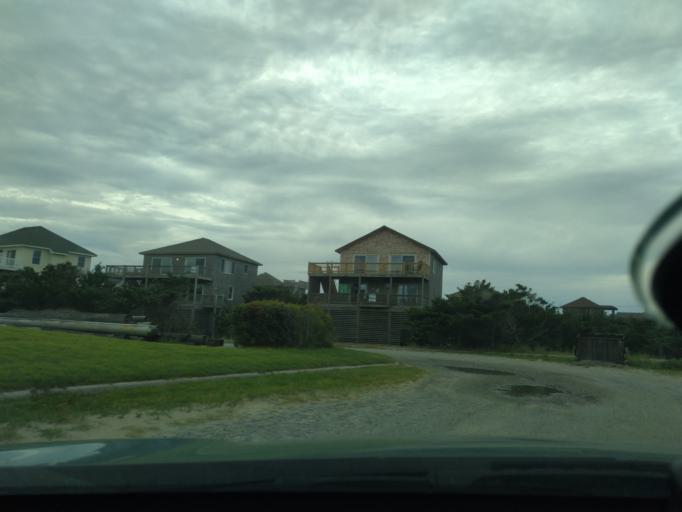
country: US
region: North Carolina
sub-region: Dare County
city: Buxton
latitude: 35.3478
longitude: -75.5021
